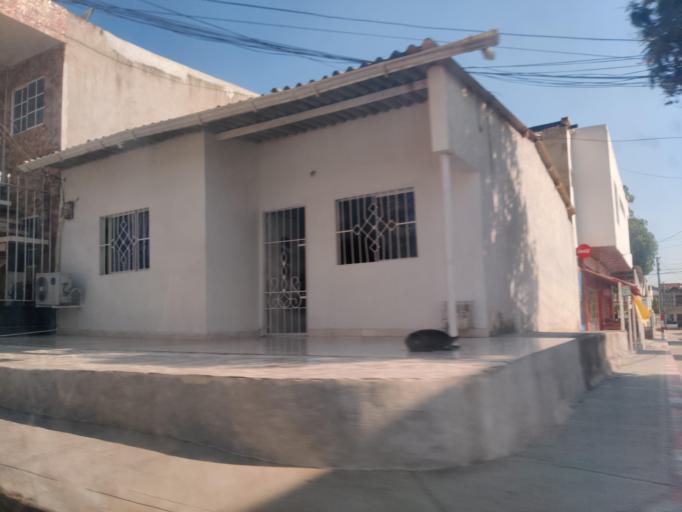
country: CO
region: Atlantico
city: Soledad
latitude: 10.9198
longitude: -74.8176
